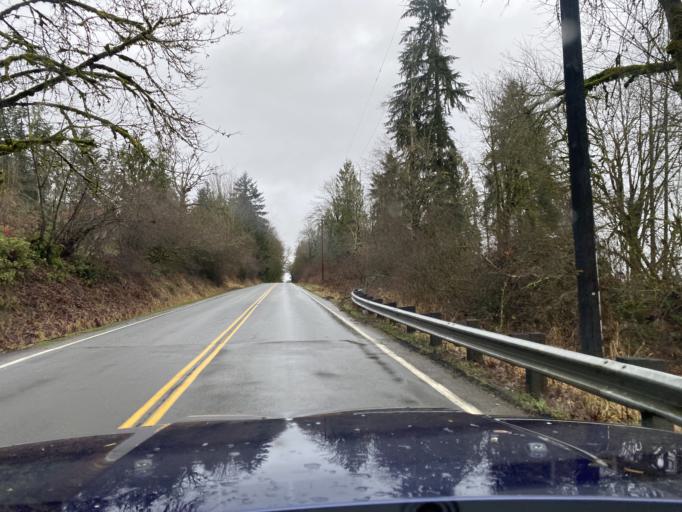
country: US
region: Washington
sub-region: King County
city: Duvall
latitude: 47.7570
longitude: -122.0045
